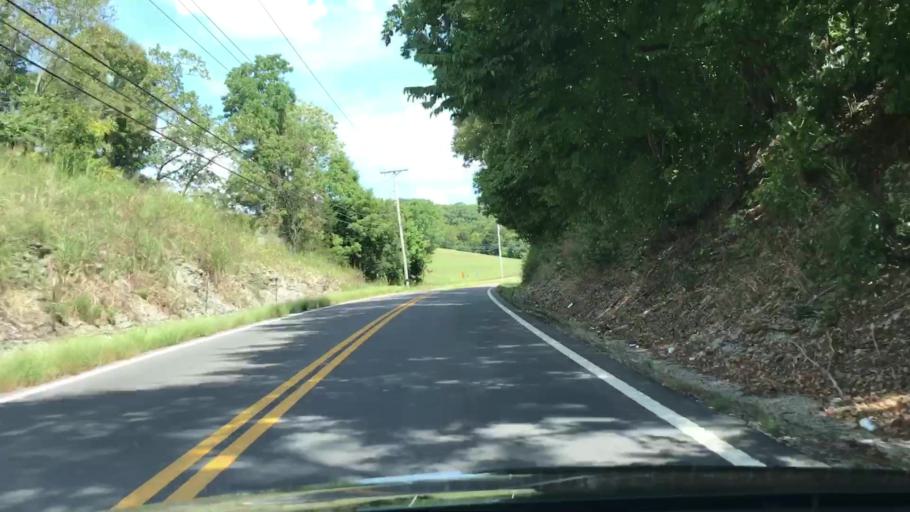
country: US
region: Tennessee
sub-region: Sumner County
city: Portland
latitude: 36.5294
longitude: -86.5438
